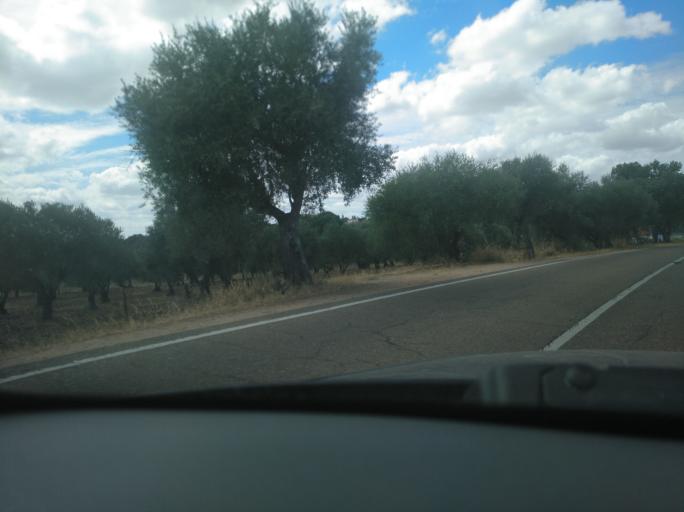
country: PT
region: Portalegre
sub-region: Arronches
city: Arronches
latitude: 39.0468
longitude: -7.4319
